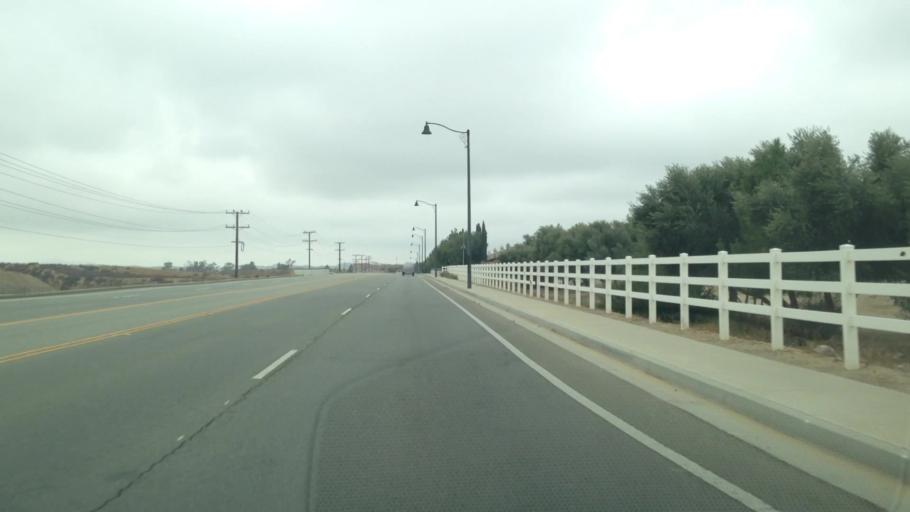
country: US
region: California
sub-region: Riverside County
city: Beaumont
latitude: 33.9470
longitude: -116.9900
